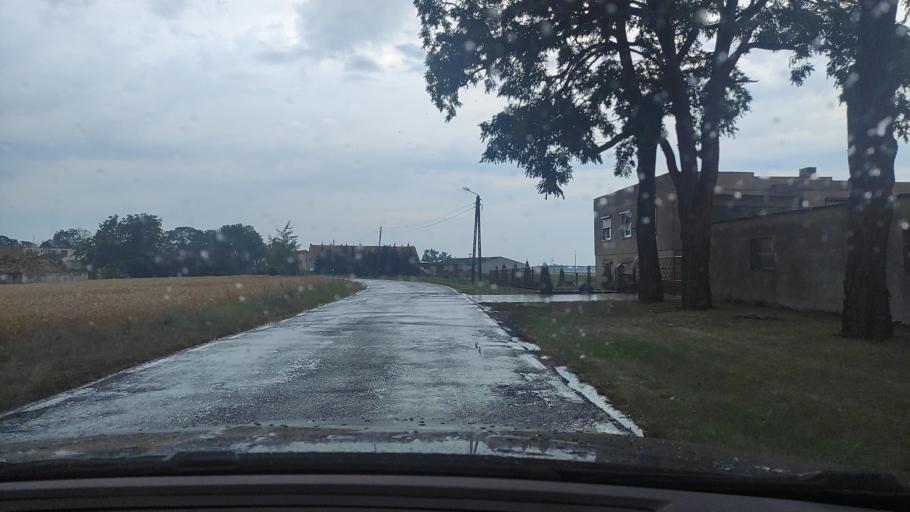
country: PL
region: Greater Poland Voivodeship
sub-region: Powiat poznanski
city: Kleszczewo
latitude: 52.2939
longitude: 17.1642
